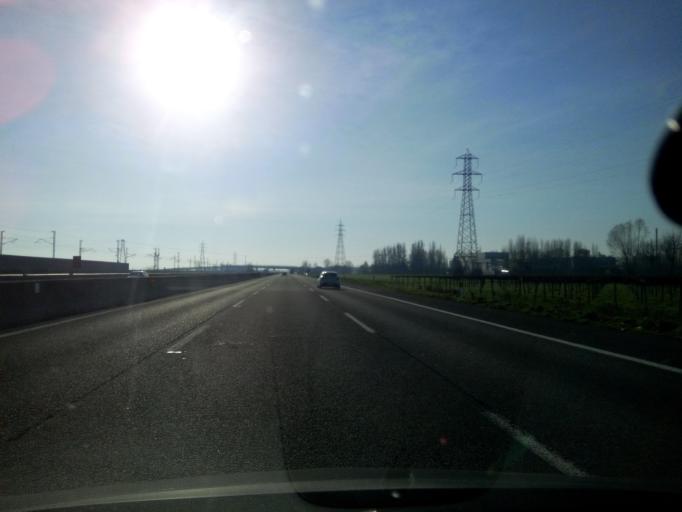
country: IT
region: Emilia-Romagna
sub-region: Provincia di Reggio Emilia
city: Prato
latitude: 44.6938
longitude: 10.7689
